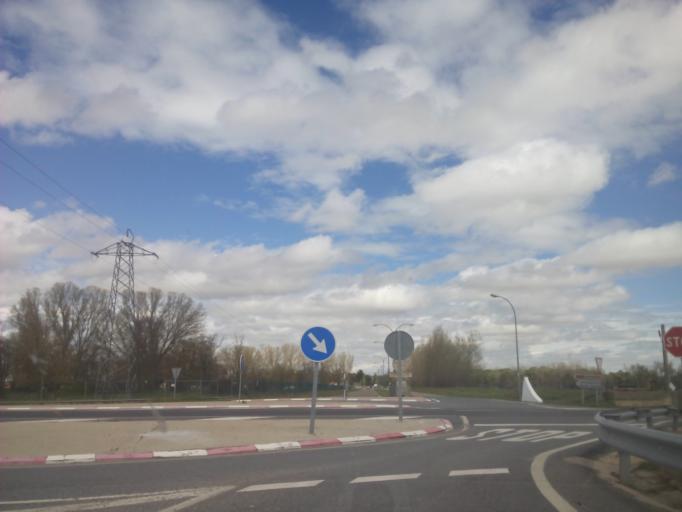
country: ES
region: Castille and Leon
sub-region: Provincia de Salamanca
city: Encinas de Abajo
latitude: 40.9369
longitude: -5.4958
